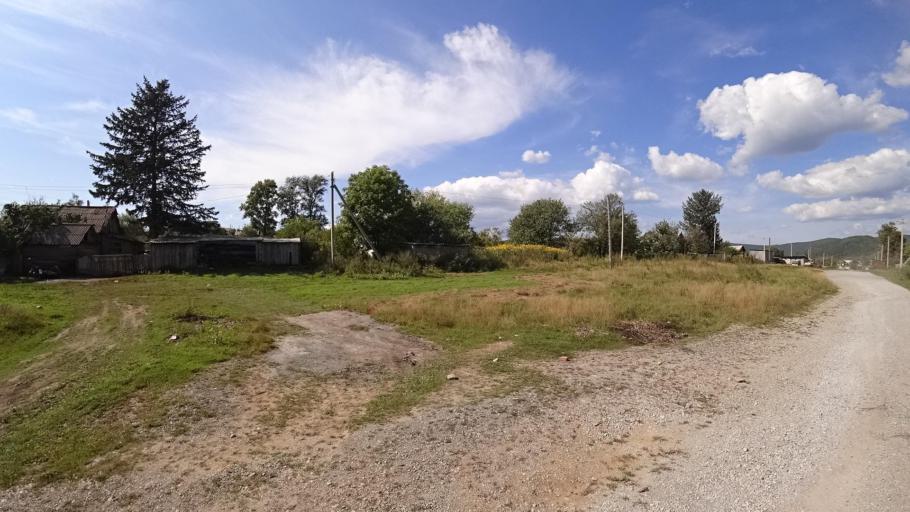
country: RU
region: Jewish Autonomous Oblast
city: Londoko
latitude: 49.0072
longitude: 131.8719
